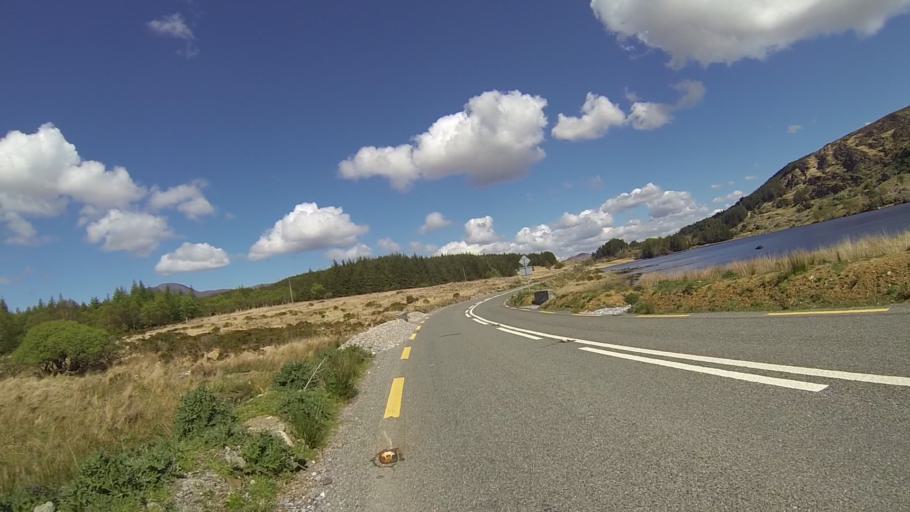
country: IE
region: Munster
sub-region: Ciarrai
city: Kenmare
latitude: 51.9570
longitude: -9.6216
